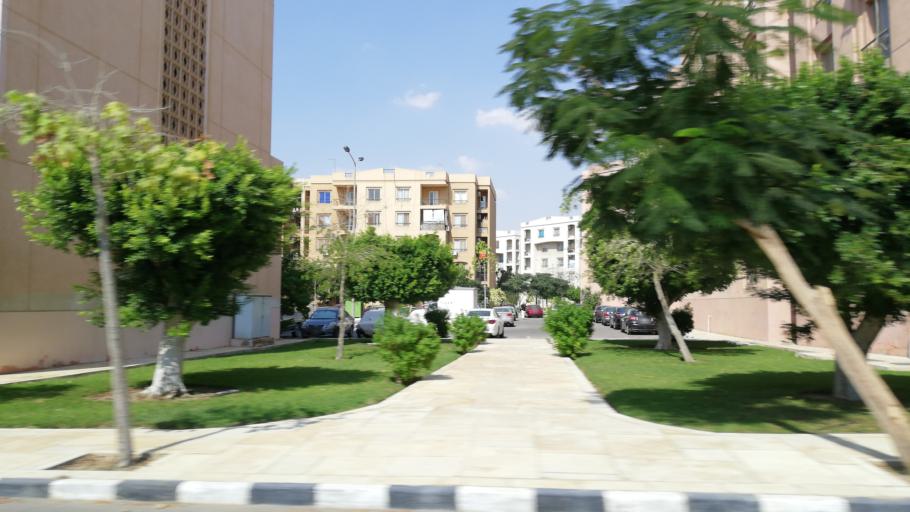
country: EG
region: Muhafazat al Qalyubiyah
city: Al Khankah
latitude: 30.0629
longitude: 31.4875
